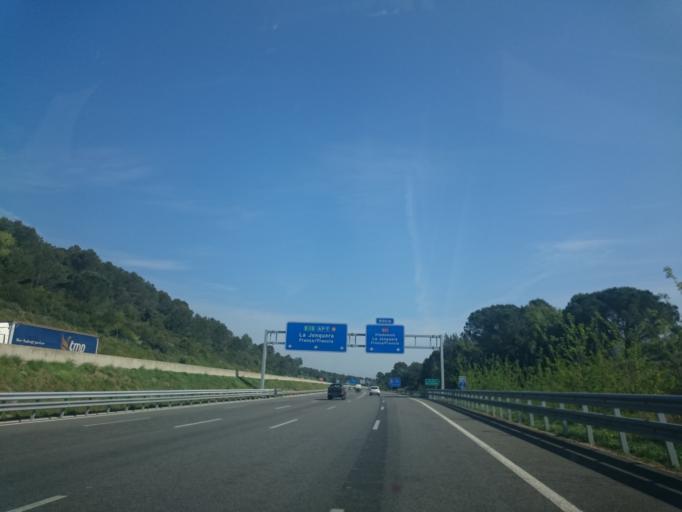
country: ES
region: Catalonia
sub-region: Provincia de Girona
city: Cervia de Ter
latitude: 42.0658
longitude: 2.8867
